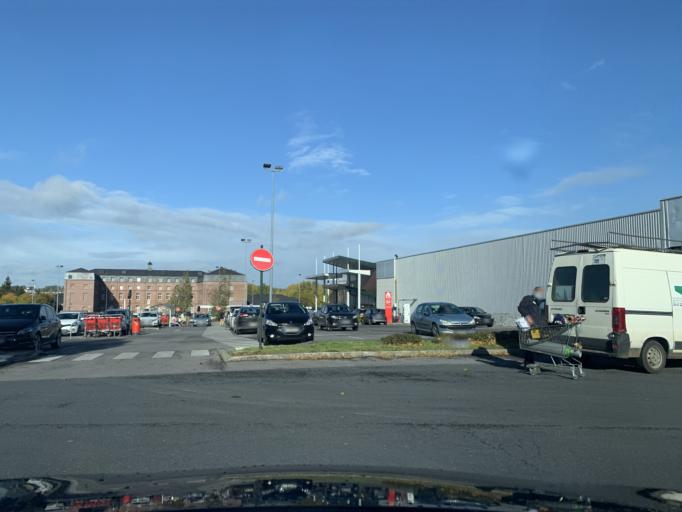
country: FR
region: Nord-Pas-de-Calais
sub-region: Departement du Nord
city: Escaudoeuvres
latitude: 50.1835
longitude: 3.2552
